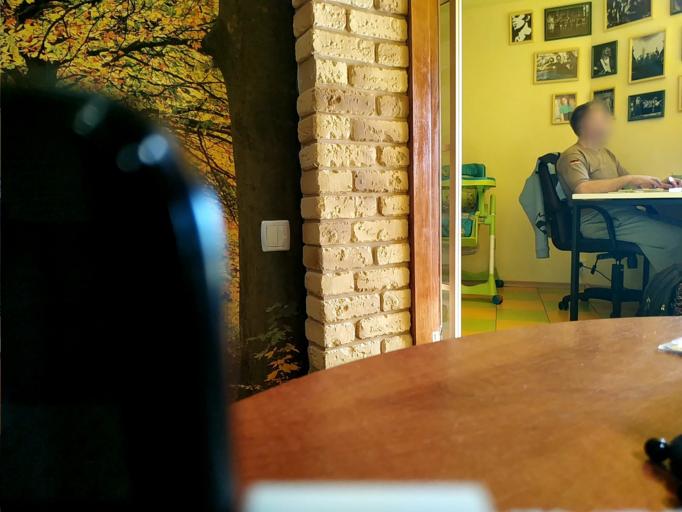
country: RU
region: Tverskaya
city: Vasil'yevskiy Mokh
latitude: 57.1159
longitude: 35.8848
